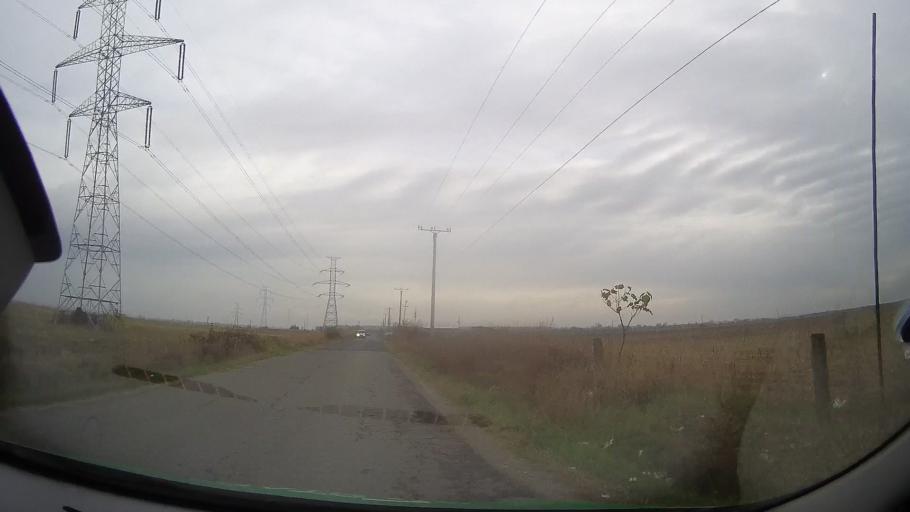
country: RO
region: Prahova
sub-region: Comuna Valea Calugareasca
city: Pantazi
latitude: 44.9279
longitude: 26.1496
